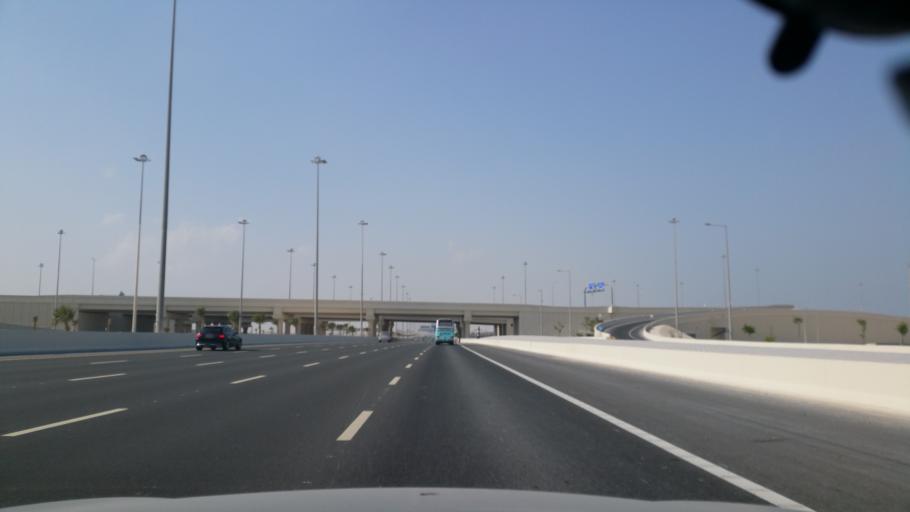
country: QA
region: Baladiyat Umm Salal
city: Umm Salal Muhammad
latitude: 25.4278
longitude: 51.4851
